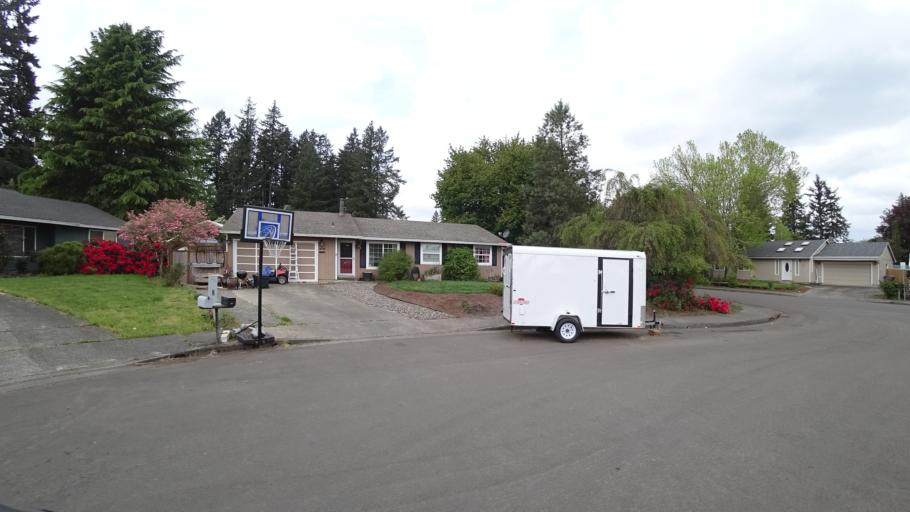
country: US
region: Oregon
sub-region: Washington County
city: Hillsboro
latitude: 45.5413
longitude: -122.9973
